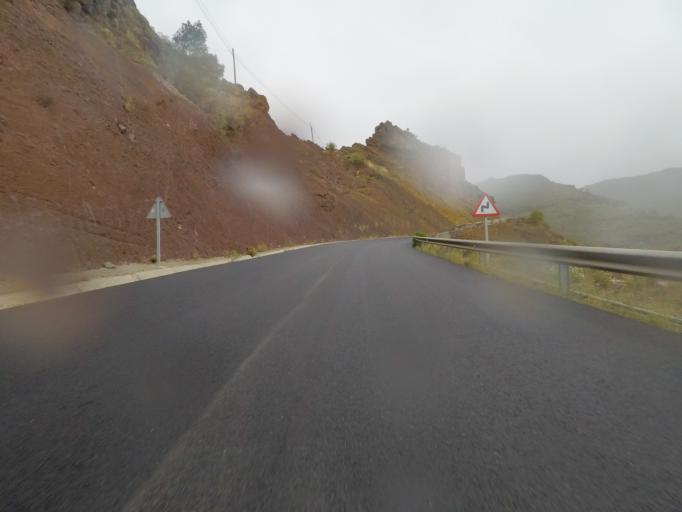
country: ES
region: Canary Islands
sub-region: Provincia de Santa Cruz de Tenerife
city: Alajero
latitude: 28.0597
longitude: -17.2028
